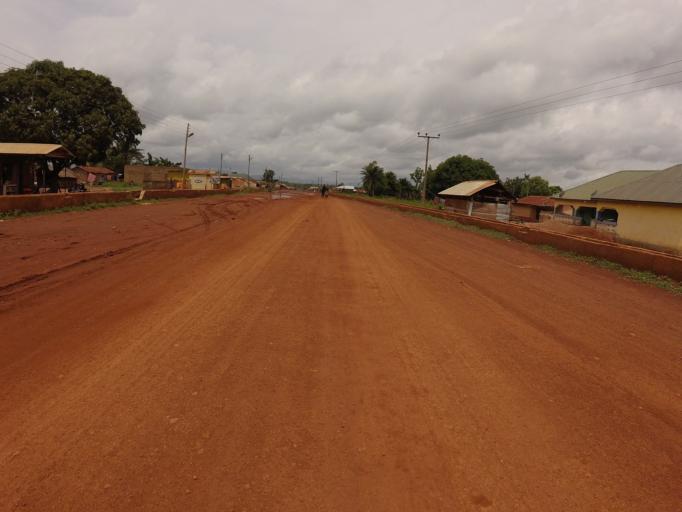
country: GH
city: Kpandae
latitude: 8.4018
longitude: 0.4033
